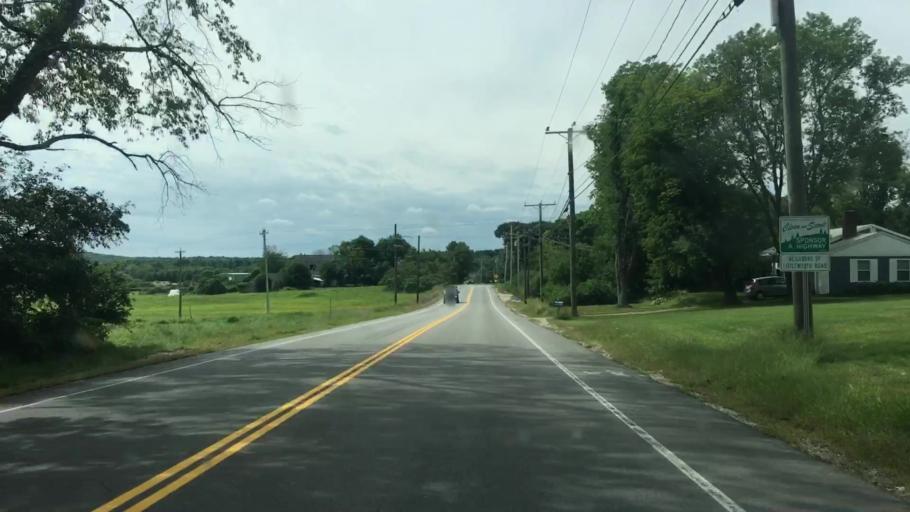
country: US
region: New Hampshire
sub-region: Strafford County
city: Madbury
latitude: 43.1886
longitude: -70.9078
